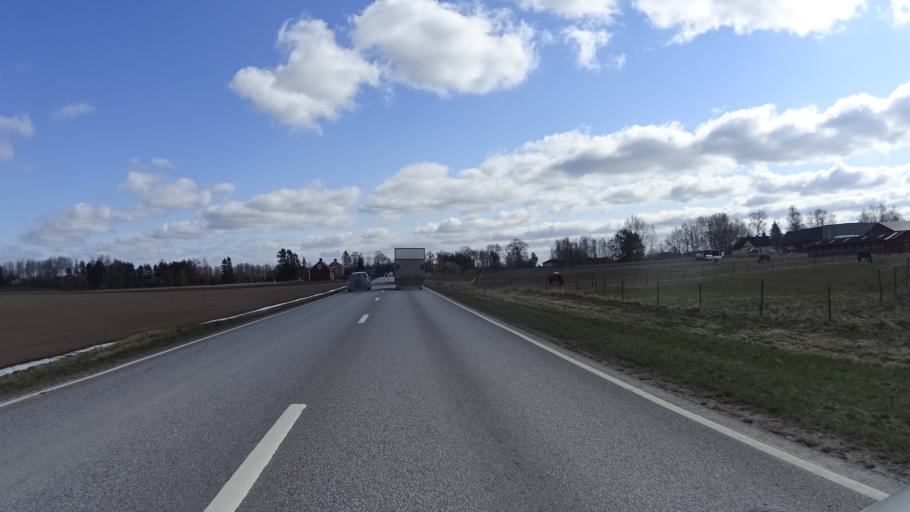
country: SE
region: OEstergoetland
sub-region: Mjolby Kommun
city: Mantorp
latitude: 58.3777
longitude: 15.2440
